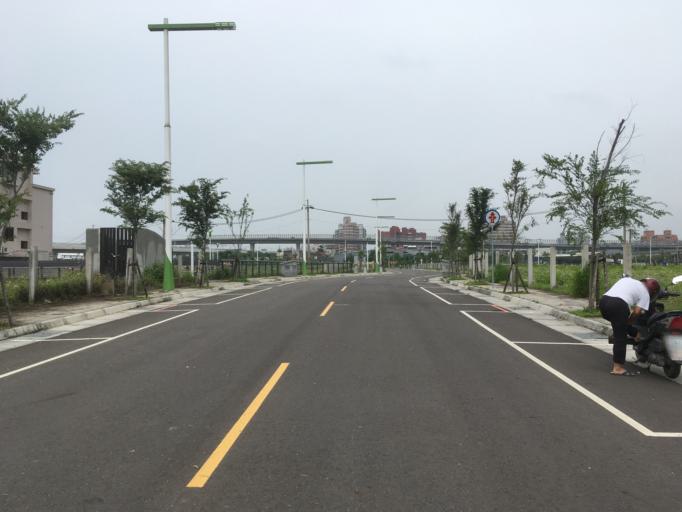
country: TW
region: Taiwan
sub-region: Taichung City
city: Taichung
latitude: 24.1957
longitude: 120.7061
